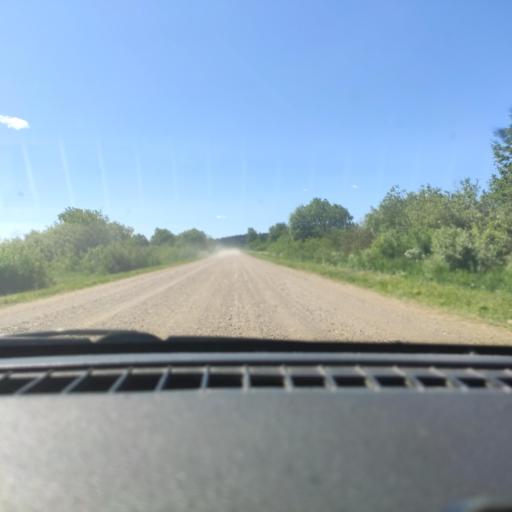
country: RU
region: Perm
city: Verkhnechusovskiye Gorodki
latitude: 58.1949
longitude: 57.1359
